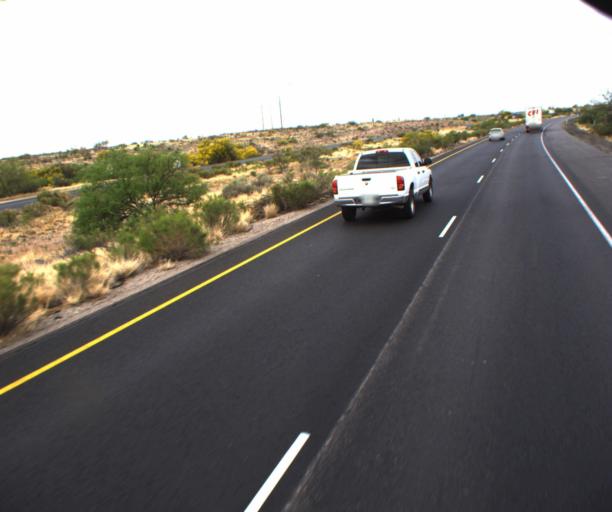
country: US
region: Arizona
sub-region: Pima County
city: Vail
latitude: 32.0024
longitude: -110.6815
